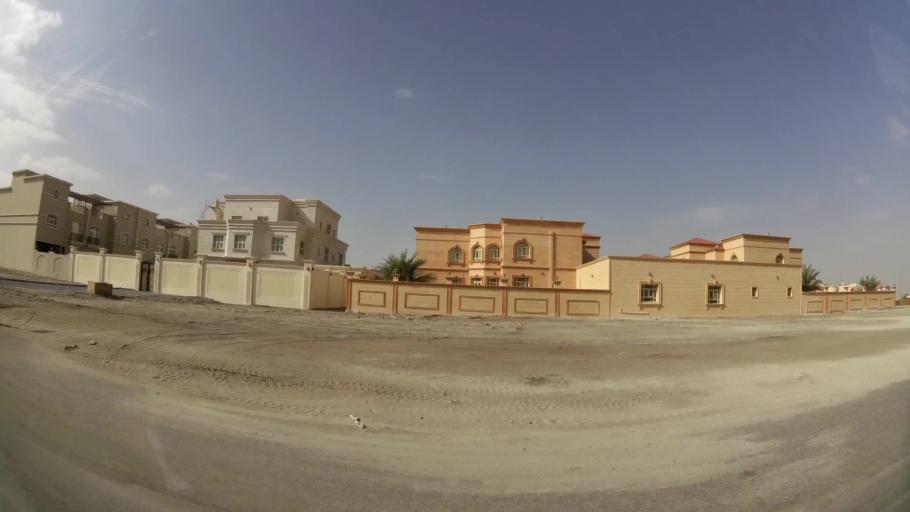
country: AE
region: Abu Dhabi
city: Abu Dhabi
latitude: 24.4215
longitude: 54.5956
